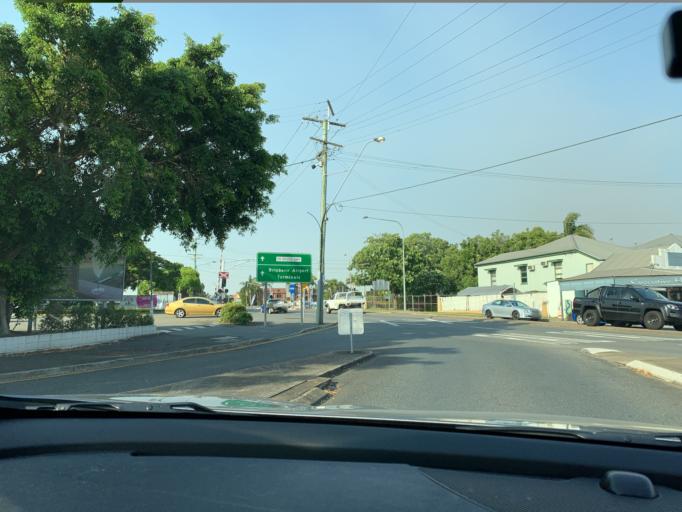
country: AU
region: Queensland
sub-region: Brisbane
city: Ascot
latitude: -27.4317
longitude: 153.0715
